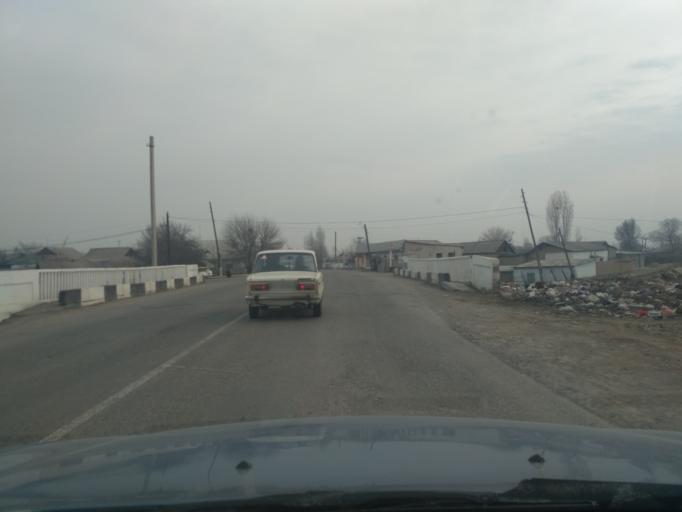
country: UZ
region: Sirdaryo
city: Sirdaryo
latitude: 40.8190
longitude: 68.6694
